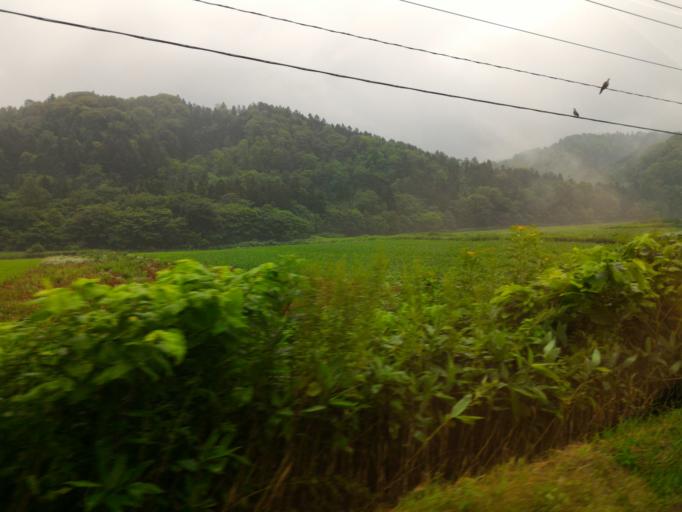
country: JP
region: Hokkaido
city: Nayoro
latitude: 44.6120
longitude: 142.3087
